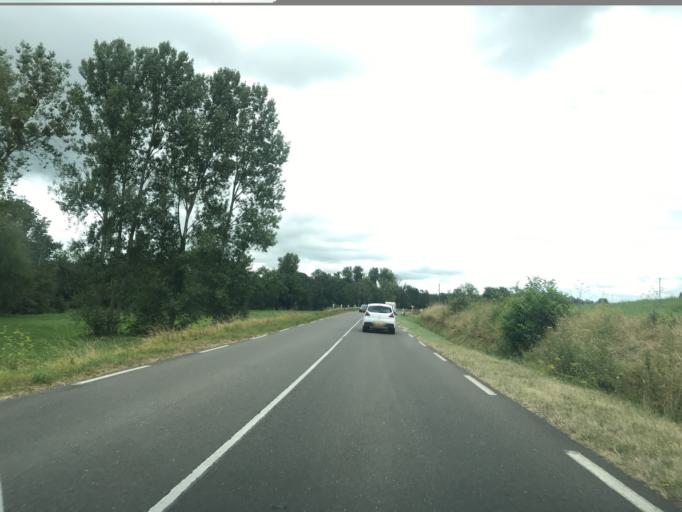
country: FR
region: Aquitaine
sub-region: Departement de la Dordogne
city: Mareuil
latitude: 45.4863
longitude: 0.3947
